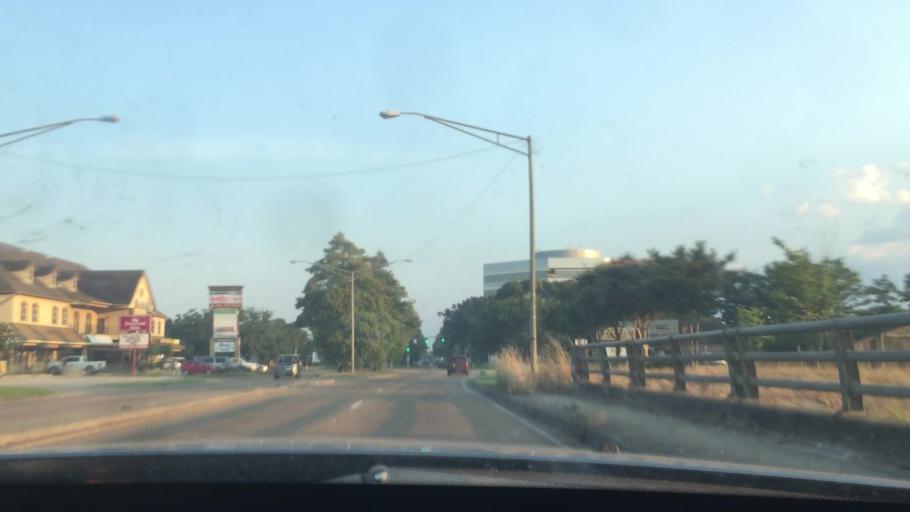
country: US
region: Louisiana
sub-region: East Baton Rouge Parish
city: Inniswold
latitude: 30.4191
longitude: -91.0516
